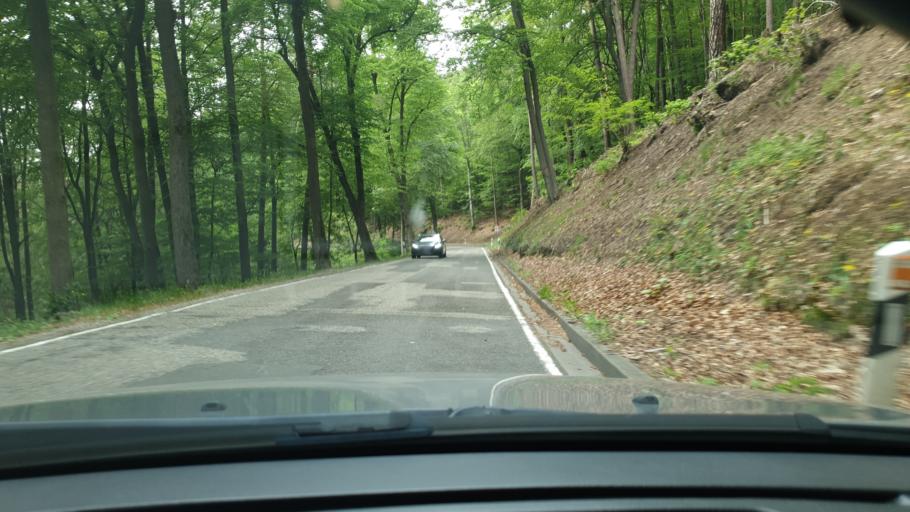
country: DE
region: Rheinland-Pfalz
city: Martinshohe
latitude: 49.3819
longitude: 7.4772
